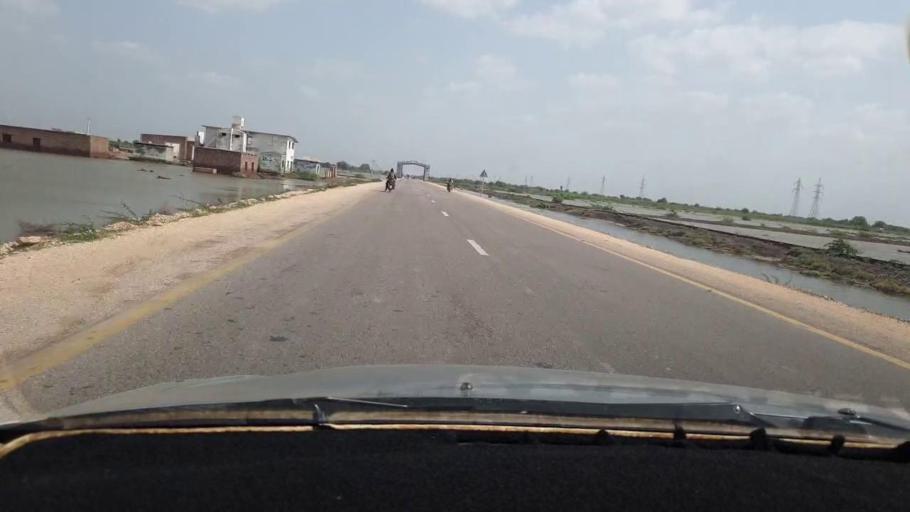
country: PK
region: Sindh
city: Digri
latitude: 25.0487
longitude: 69.2258
